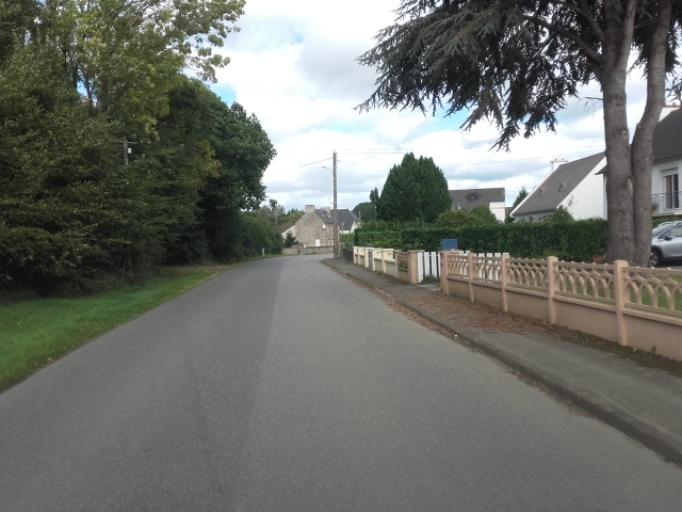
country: FR
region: Brittany
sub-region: Departement des Cotes-d'Armor
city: Lanvollon
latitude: 48.6257
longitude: -2.9861
